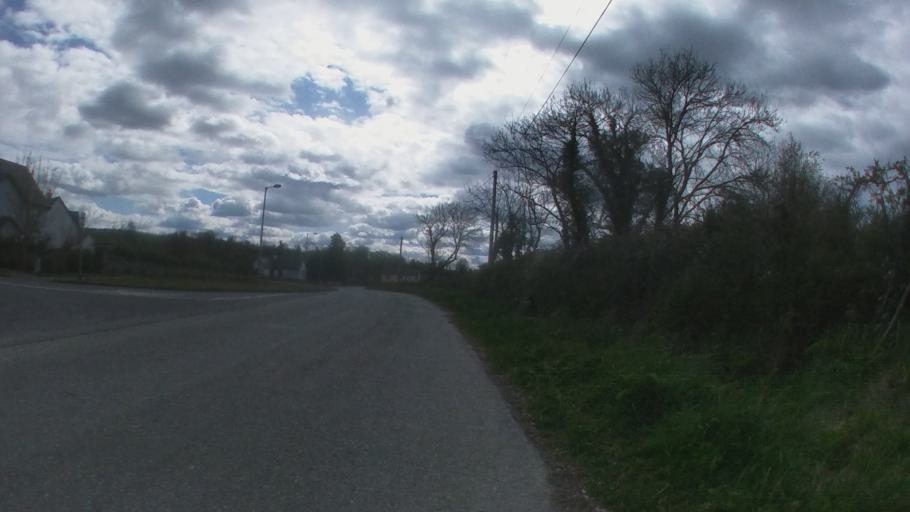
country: IE
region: Leinster
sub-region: Kilkenny
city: Kilkenny
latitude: 52.7191
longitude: -7.2342
